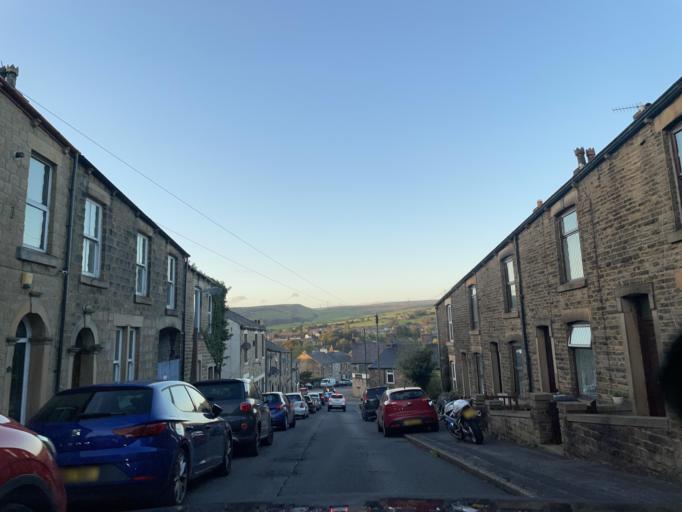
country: GB
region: England
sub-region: Borough of Tameside
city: Longdendale
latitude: 53.4638
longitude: -1.9710
